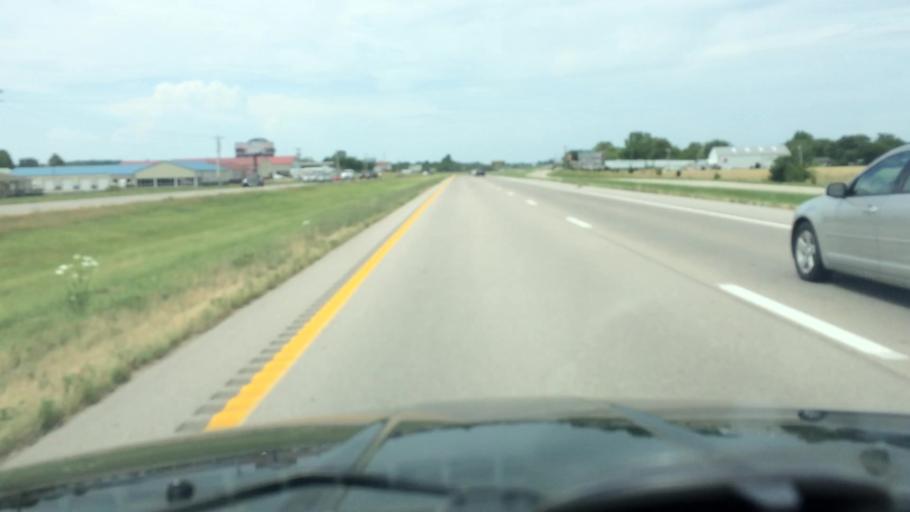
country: US
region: Missouri
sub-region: Polk County
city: Bolivar
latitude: 37.5601
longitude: -93.3911
